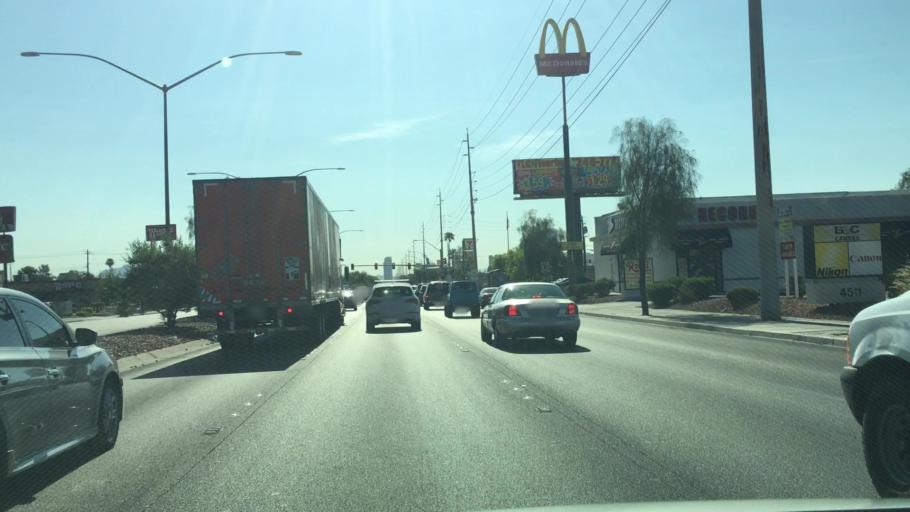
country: US
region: Nevada
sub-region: Clark County
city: Spring Valley
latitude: 36.1444
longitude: -115.2018
